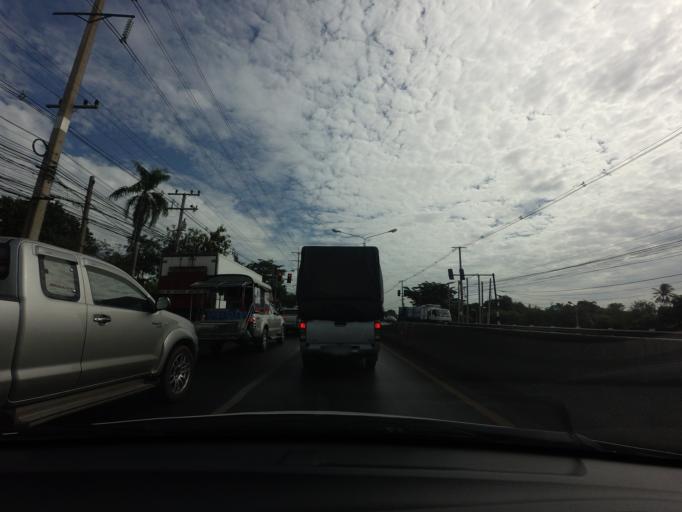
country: TH
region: Pathum Thani
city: Thanyaburi
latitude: 14.0202
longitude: 100.7346
